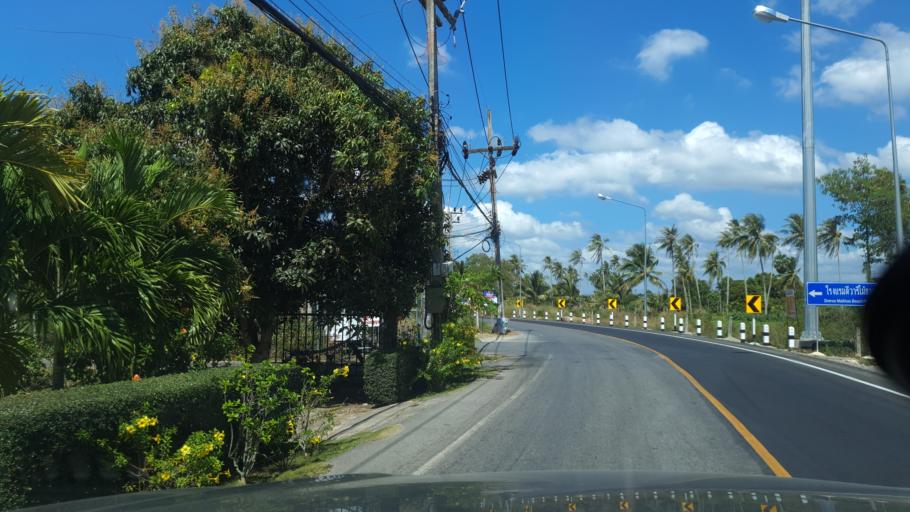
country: TH
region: Phuket
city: Thalang
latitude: 8.1424
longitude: 98.3065
